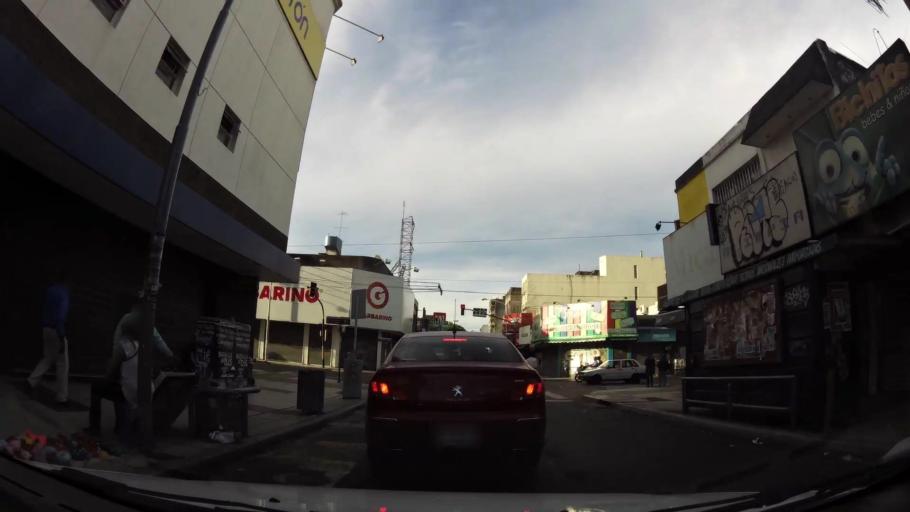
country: AR
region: Buenos Aires
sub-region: Partido de Moron
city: Moron
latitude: -34.6495
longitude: -58.6211
